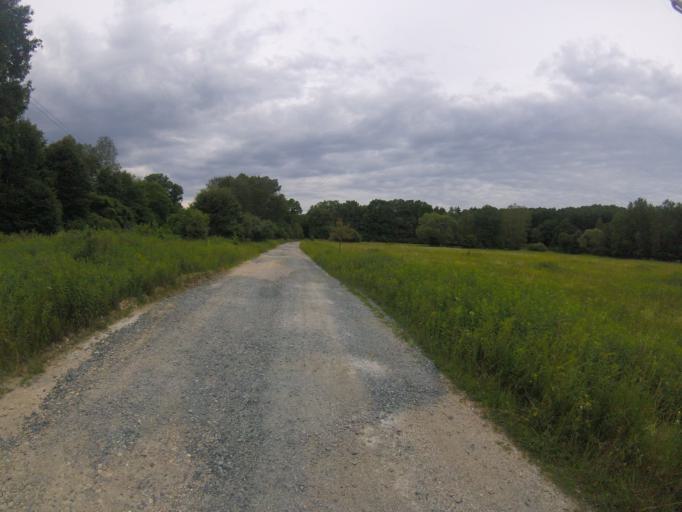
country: SI
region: Hodos-Hodos
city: Hodos
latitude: 46.8371
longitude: 16.4381
